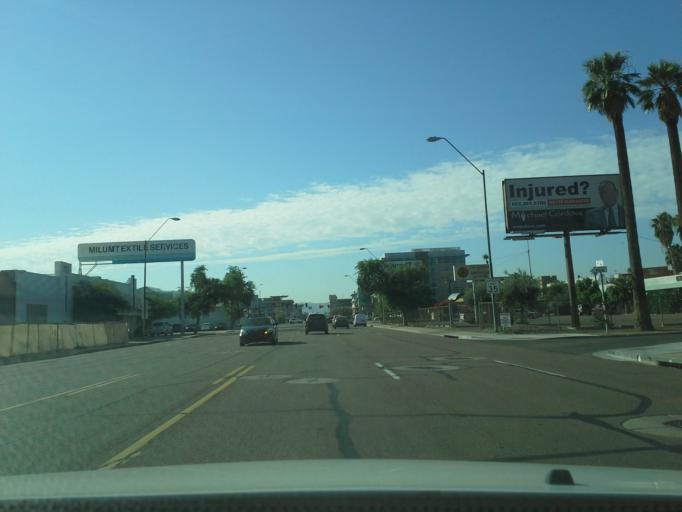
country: US
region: Arizona
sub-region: Maricopa County
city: Phoenix
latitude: 33.4536
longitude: -112.0826
